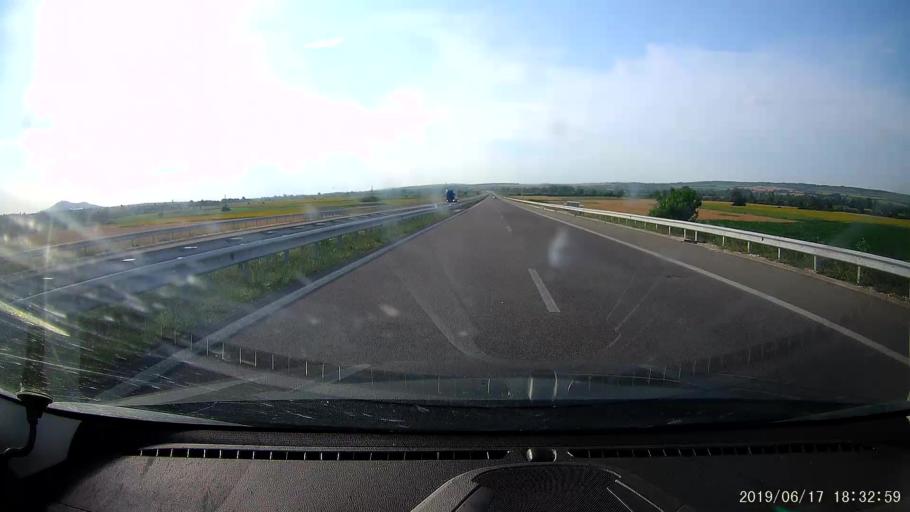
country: BG
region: Khaskovo
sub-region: Obshtina Dimitrovgrad
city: Dimitrovgrad
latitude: 42.0702
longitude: 25.4671
